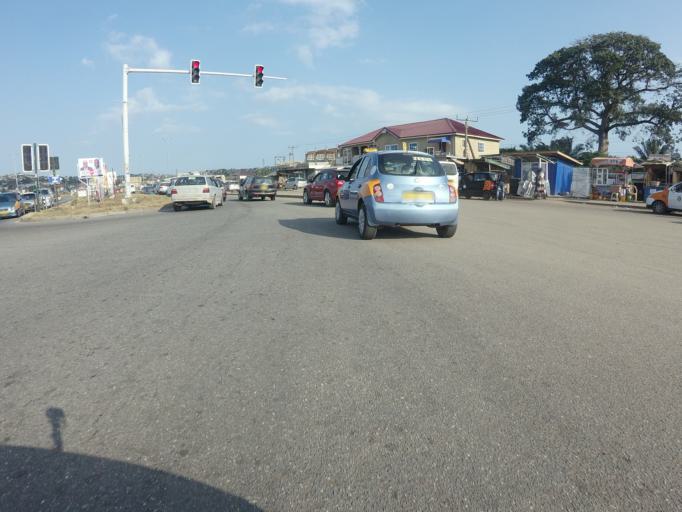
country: GH
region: Greater Accra
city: Gbawe
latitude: 5.6274
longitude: -0.3121
